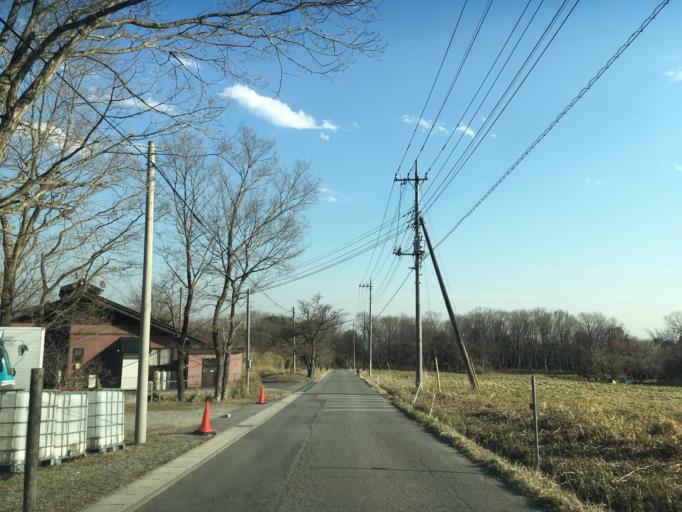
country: JP
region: Tochigi
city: Kuroiso
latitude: 37.0678
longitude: 140.0034
